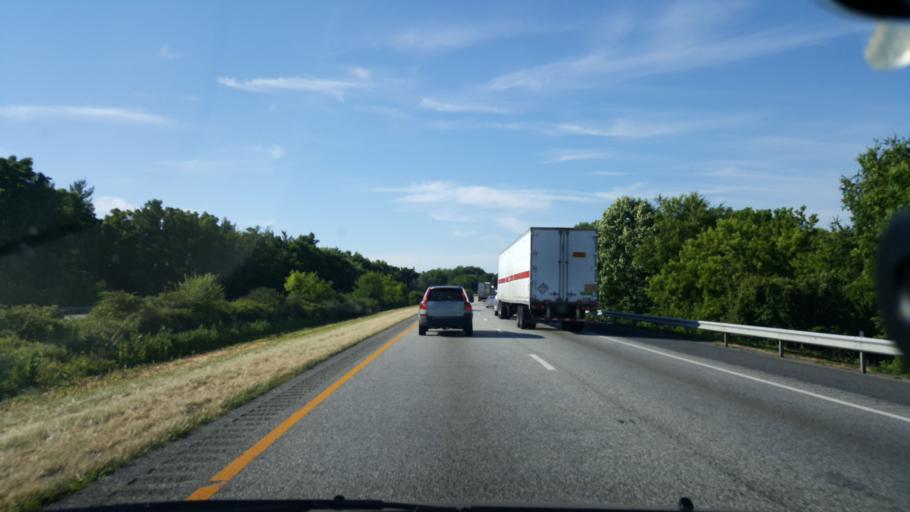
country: US
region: Virginia
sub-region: Augusta County
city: Weyers Cave
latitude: 38.3410
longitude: -78.9338
